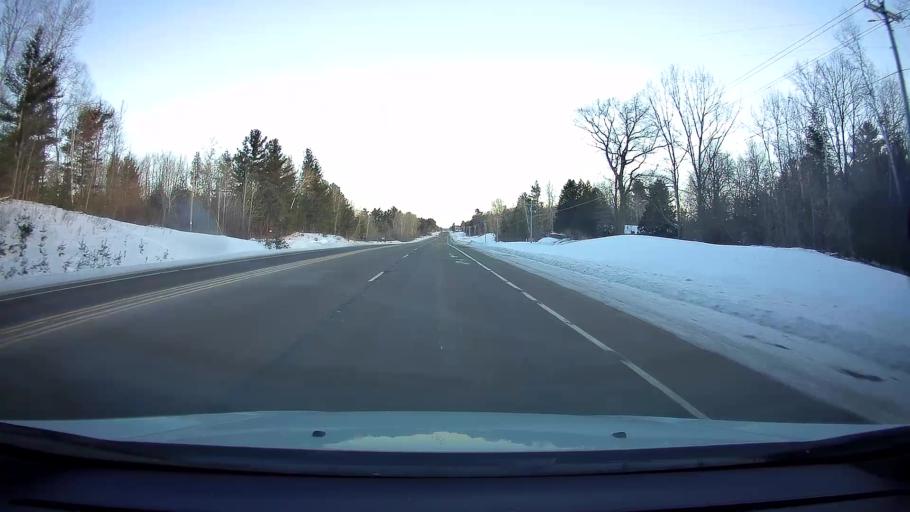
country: US
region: Wisconsin
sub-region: Barron County
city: Cumberland
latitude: 45.5626
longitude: -92.0172
